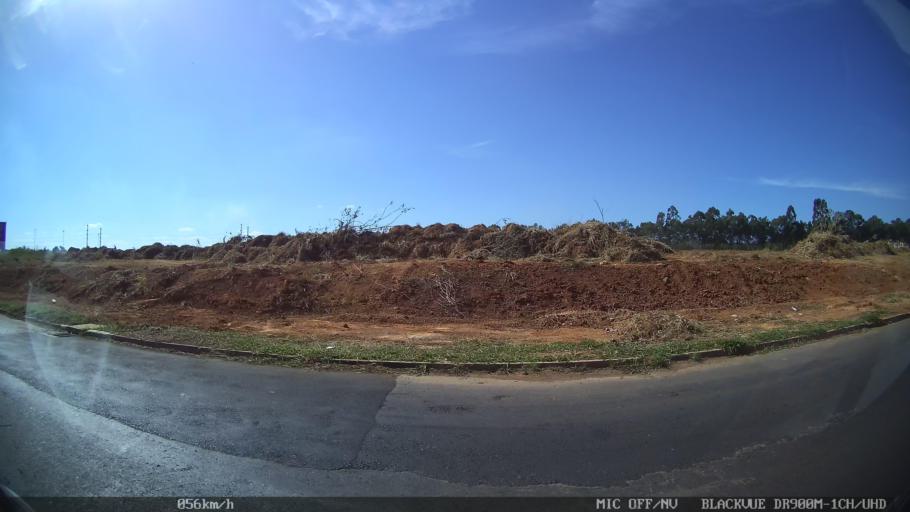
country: BR
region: Sao Paulo
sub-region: Franca
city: Franca
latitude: -20.4798
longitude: -47.4070
